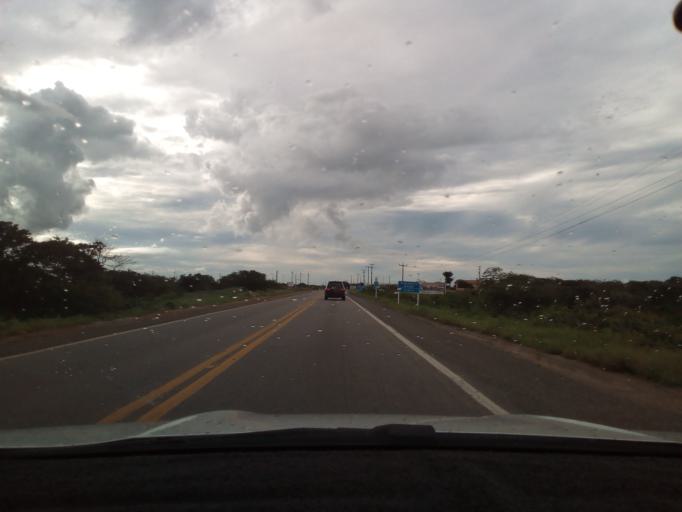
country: BR
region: Ceara
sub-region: Aracati
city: Aracati
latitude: -4.6249
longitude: -37.6459
